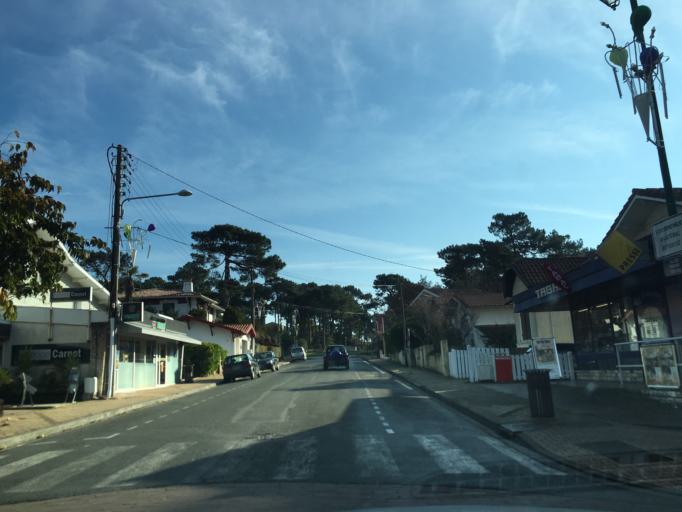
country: FR
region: Aquitaine
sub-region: Departement de la Gironde
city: Arcachon
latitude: 44.6482
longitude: -1.1853
